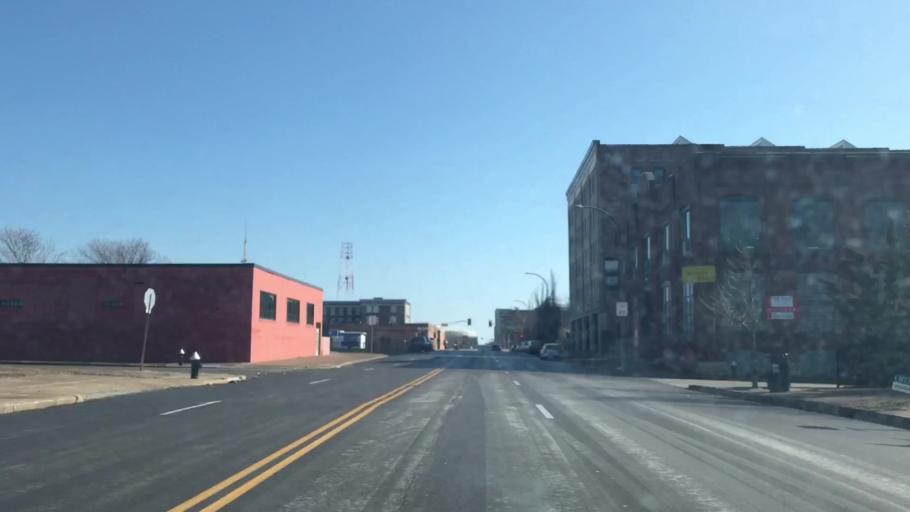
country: US
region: Missouri
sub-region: City of Saint Louis
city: St. Louis
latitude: 38.6360
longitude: -90.2090
